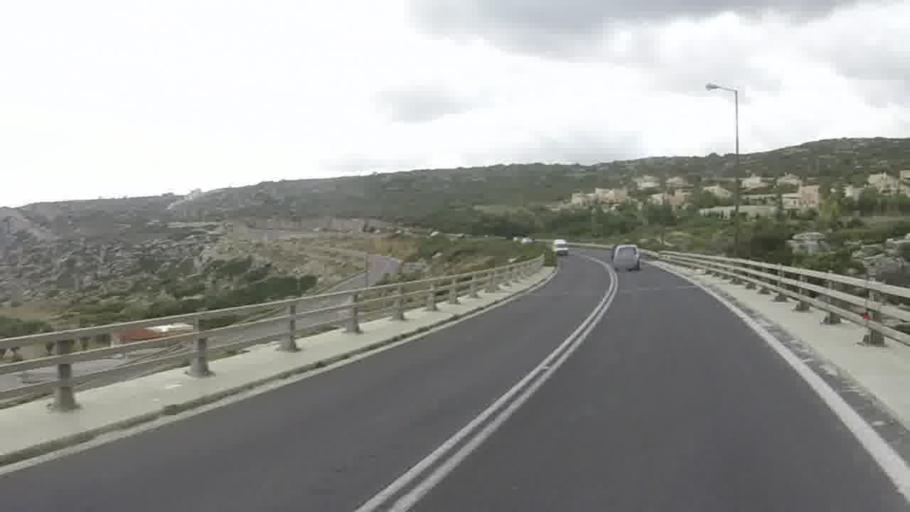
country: GR
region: Crete
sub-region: Nomos Rethymnis
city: Atsipopoulon
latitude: 35.3591
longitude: 24.4065
